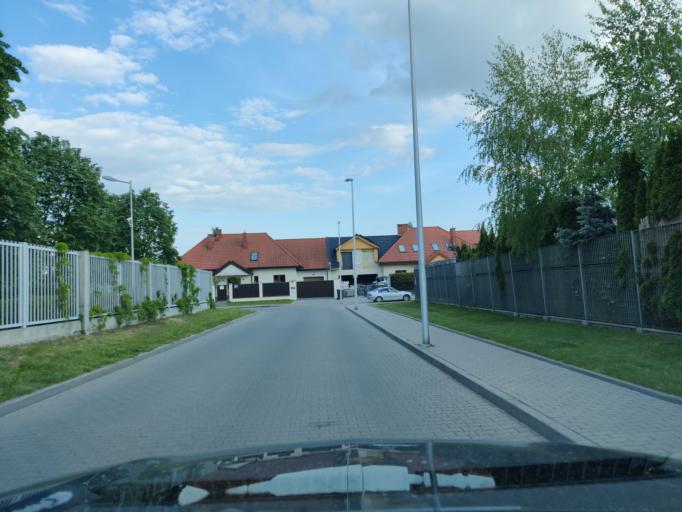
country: PL
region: Masovian Voivodeship
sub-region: Powiat piaseczynski
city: Konstancin-Jeziorna
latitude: 52.1091
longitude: 21.1100
